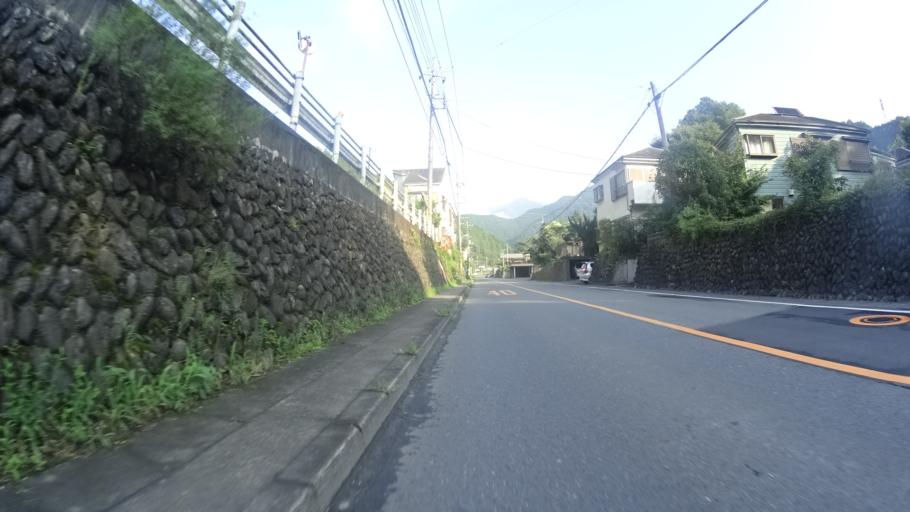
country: JP
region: Tokyo
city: Ome
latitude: 35.8090
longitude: 139.1569
